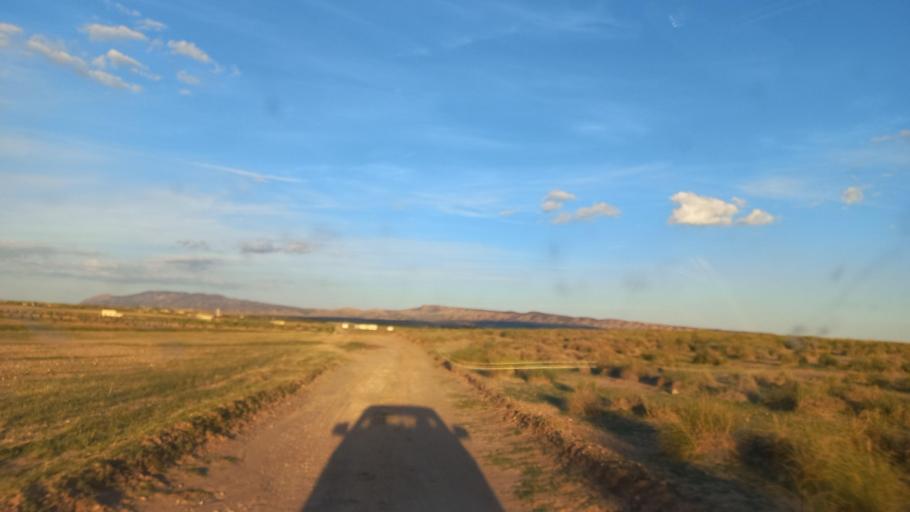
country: TN
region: Al Qasrayn
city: Sbiba
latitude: 35.3480
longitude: 9.0305
